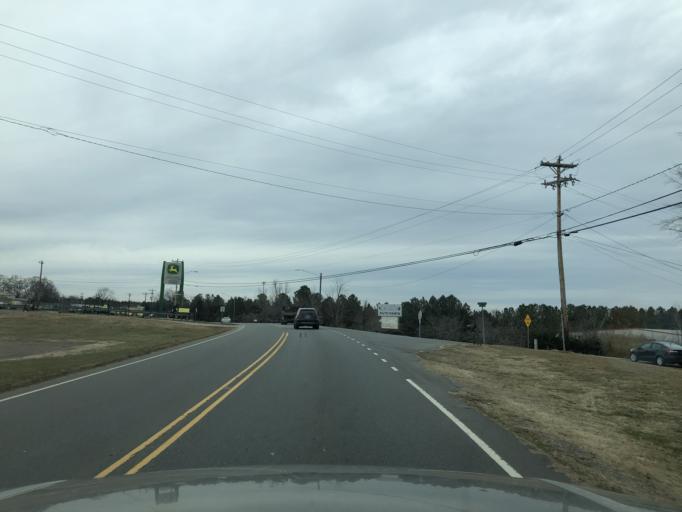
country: US
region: North Carolina
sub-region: Cleveland County
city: Shelby
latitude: 35.2974
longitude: -81.4860
